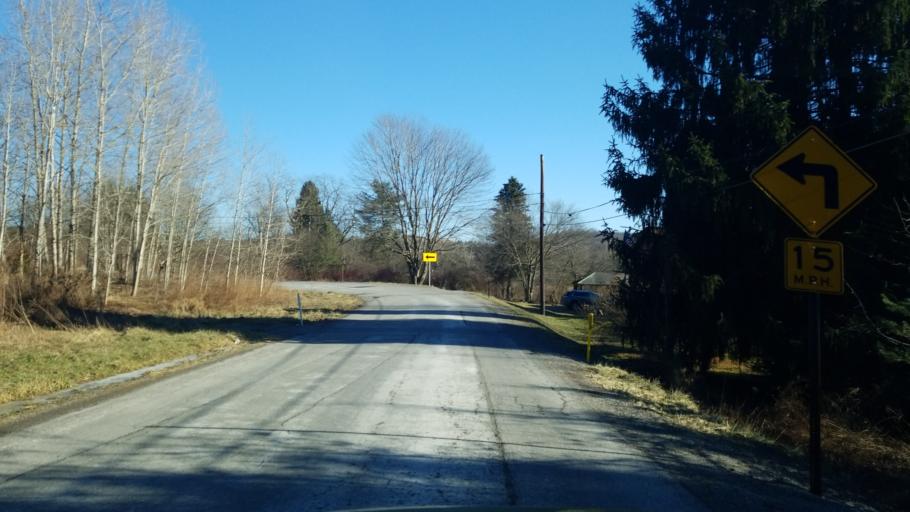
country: US
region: Pennsylvania
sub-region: Jefferson County
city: Sykesville
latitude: 41.0473
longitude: -78.7731
